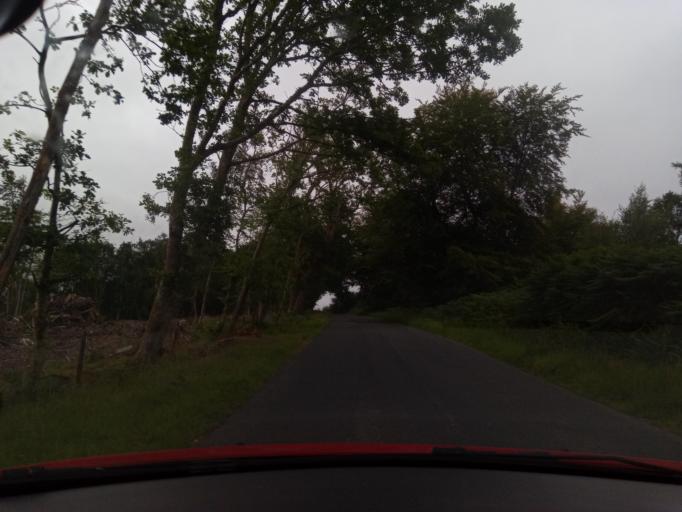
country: GB
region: England
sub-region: Northumberland
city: Otterburn
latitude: 55.3289
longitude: -2.0836
